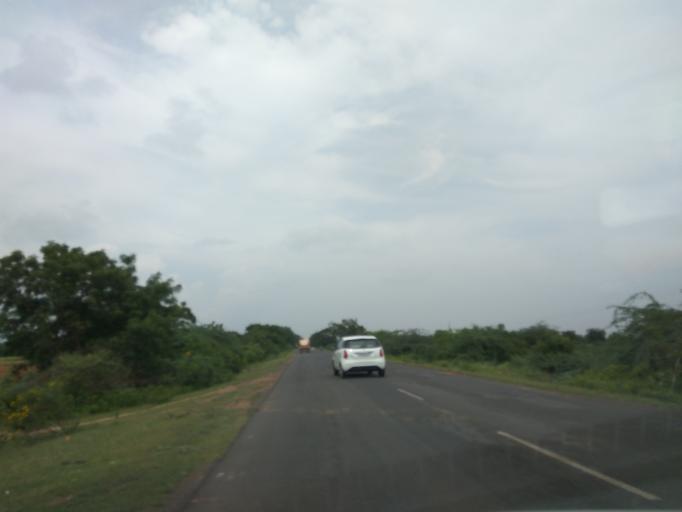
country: IN
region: Andhra Pradesh
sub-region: Prakasam
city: Cumbum
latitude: 15.5084
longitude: 79.0874
